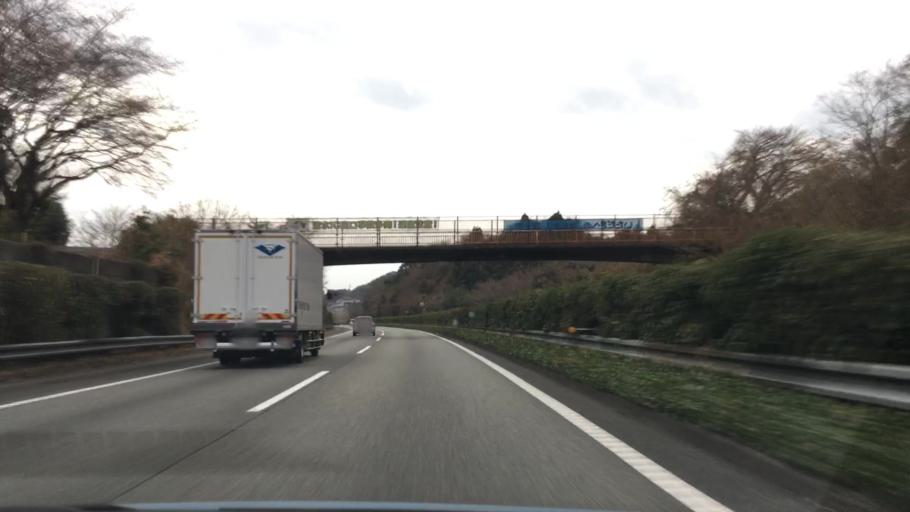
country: JP
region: Shizuoka
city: Fujinomiya
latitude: 35.1456
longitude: 138.6140
